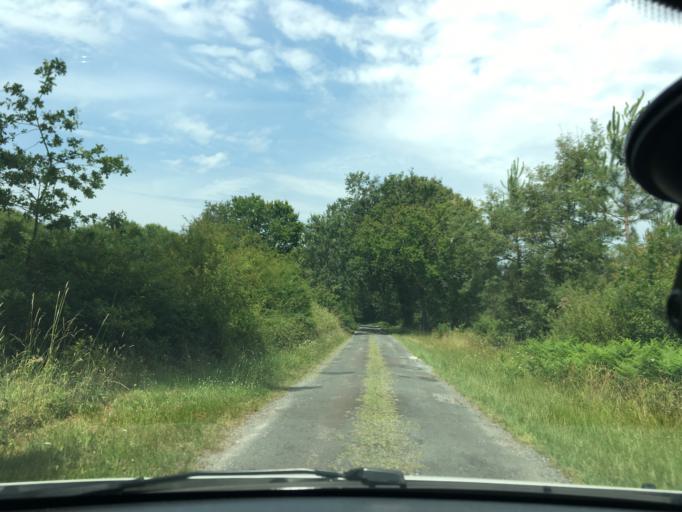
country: FR
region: Aquitaine
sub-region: Departement de la Gironde
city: Lesparre-Medoc
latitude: 45.2799
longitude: -0.9074
